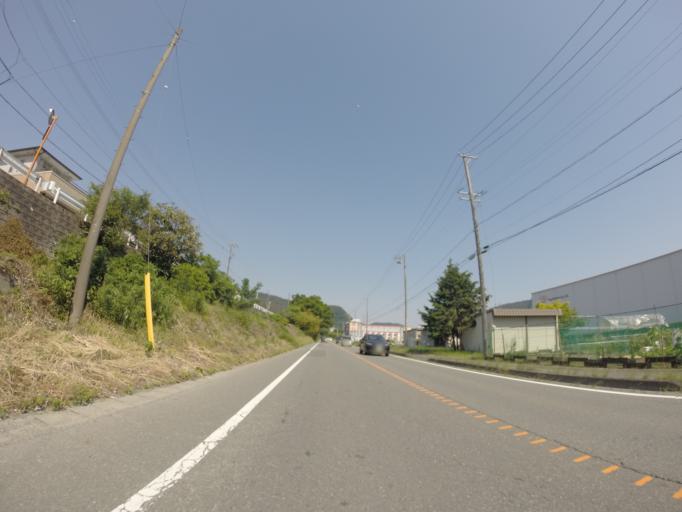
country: JP
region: Shizuoka
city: Fujinomiya
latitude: 35.1878
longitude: 138.5966
